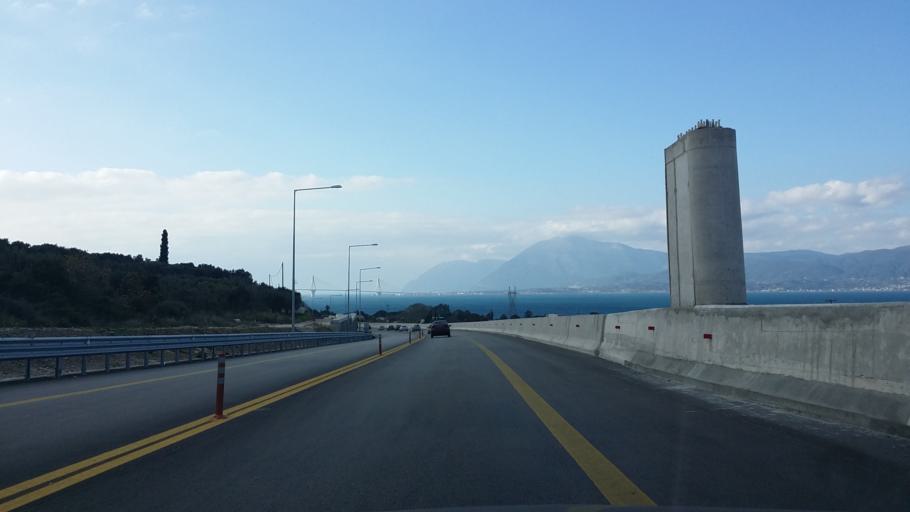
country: GR
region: West Greece
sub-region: Nomos Achaias
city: Ano Kastritsion
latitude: 38.3234
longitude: 21.8456
